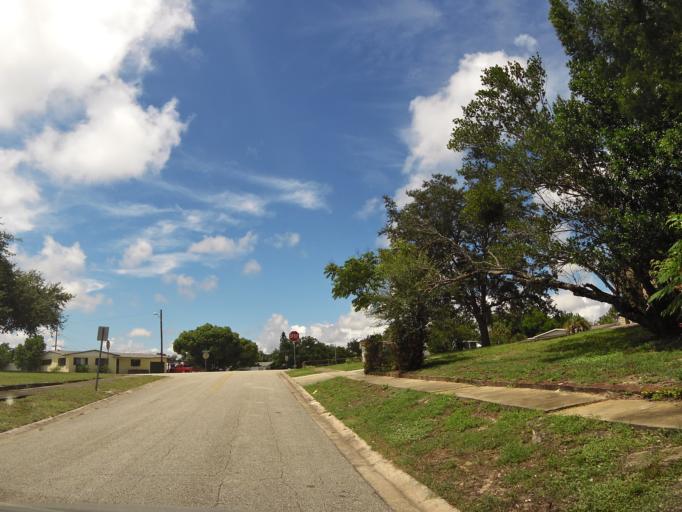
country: US
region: Florida
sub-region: Brevard County
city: Titusville
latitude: 28.6202
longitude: -80.8477
